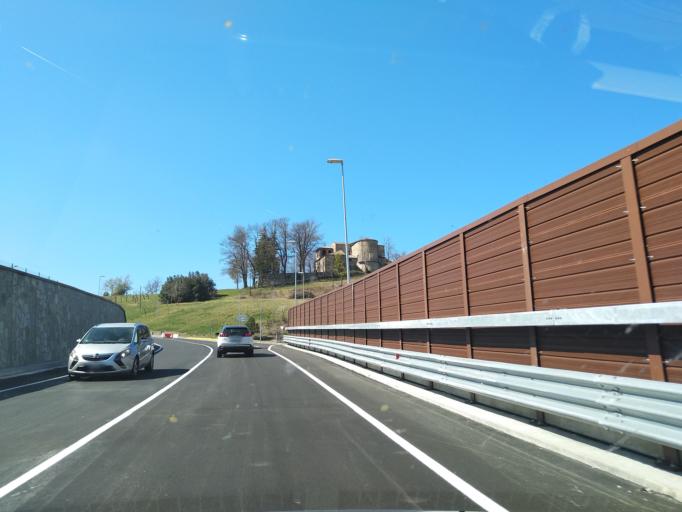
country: IT
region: Emilia-Romagna
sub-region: Provincia di Reggio Emilia
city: Castelnovo ne'Monti
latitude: 44.4331
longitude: 10.4137
